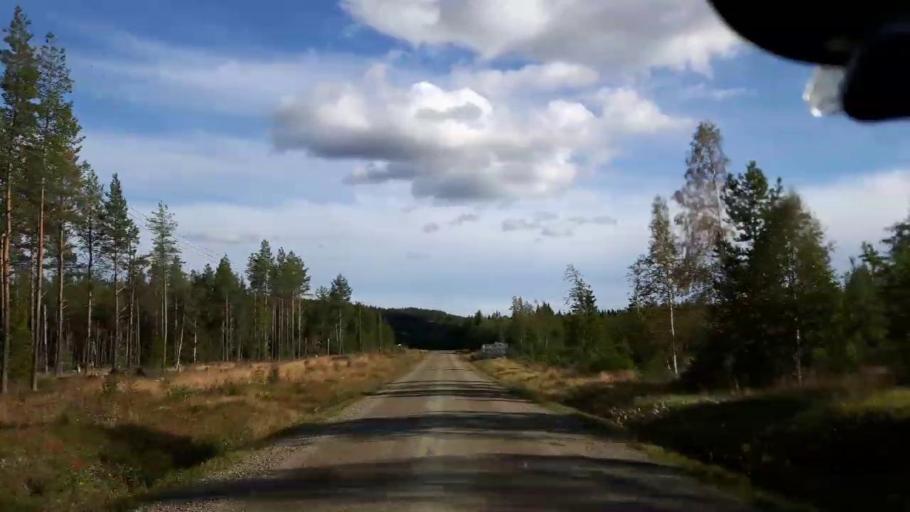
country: SE
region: Jaemtland
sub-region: Ragunda Kommun
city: Hammarstrand
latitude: 63.4266
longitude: 16.0554
